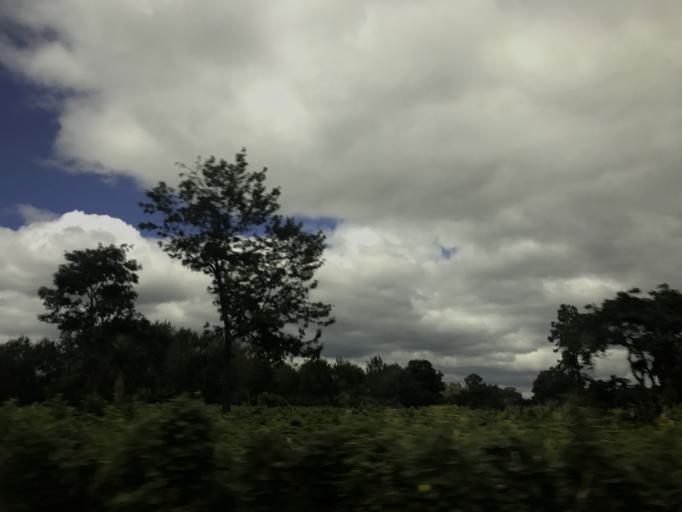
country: GT
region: Chimaltenango
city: El Tejar
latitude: 14.6286
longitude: -90.7952
